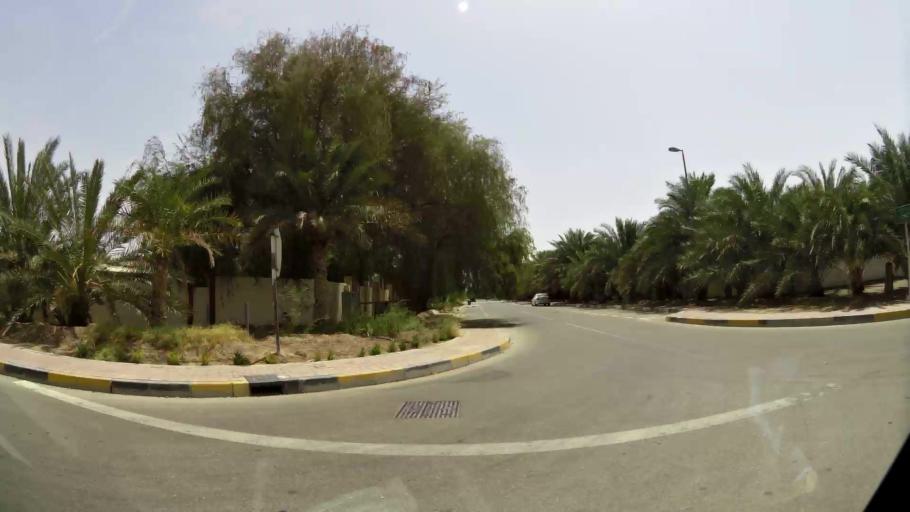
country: AE
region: Abu Dhabi
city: Al Ain
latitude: 24.1796
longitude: 55.7238
